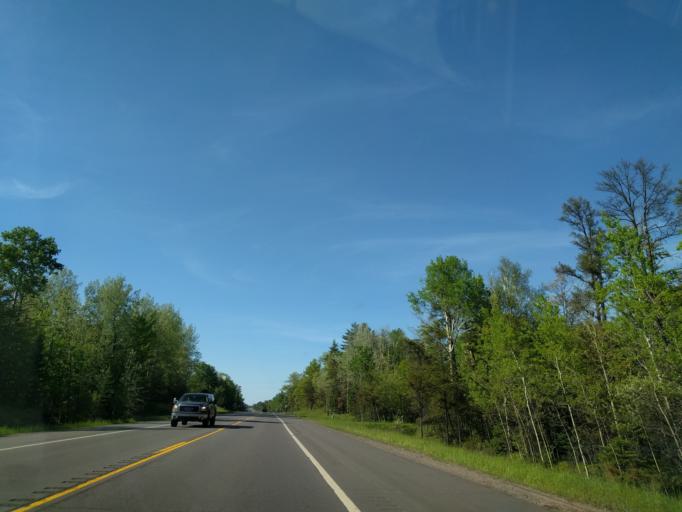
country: US
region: Michigan
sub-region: Marquette County
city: K. I. Sawyer Air Force Base
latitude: 46.3853
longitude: -87.4074
